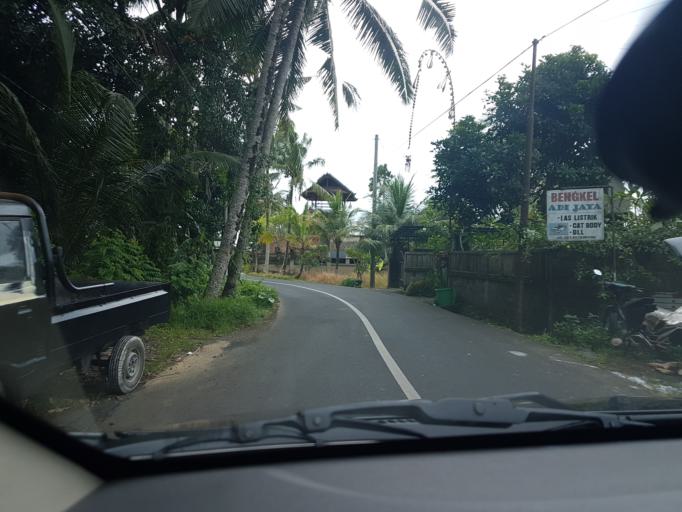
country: ID
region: Bali
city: Banjar Triwangsakeliki
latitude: -8.4593
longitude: 115.2744
